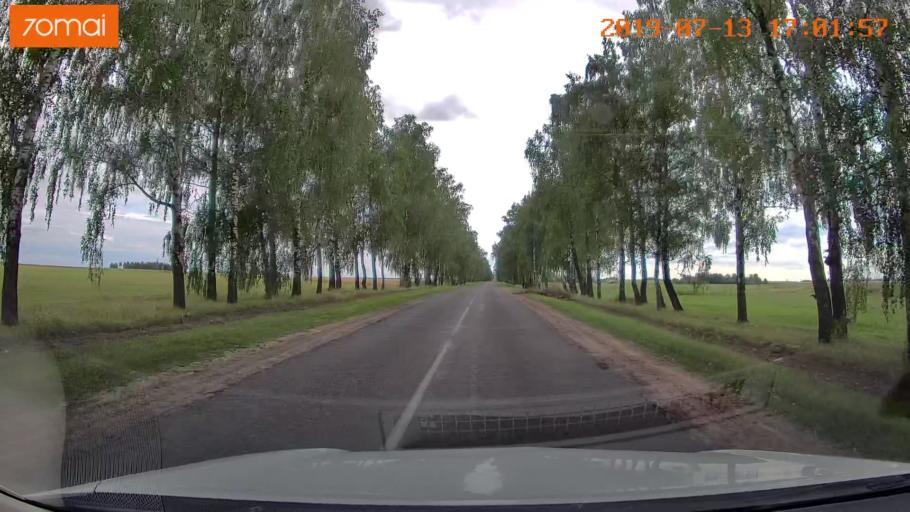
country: BY
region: Mogilev
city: Kirawsk
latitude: 53.2908
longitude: 29.3917
